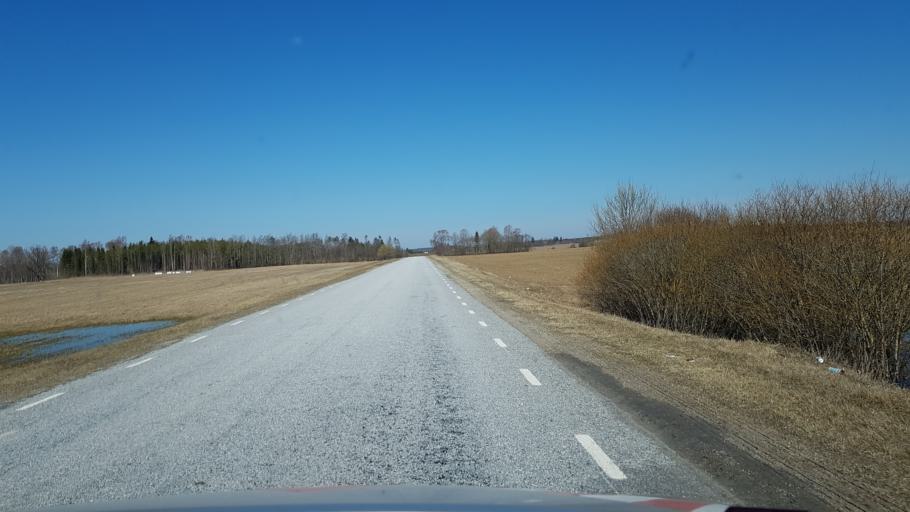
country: EE
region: Jaervamaa
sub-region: Koeru vald
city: Koeru
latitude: 59.0193
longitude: 26.0882
